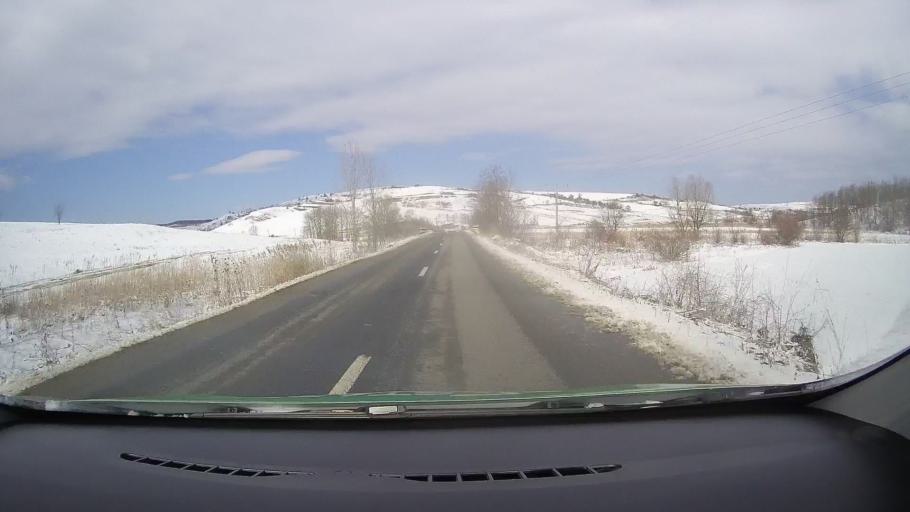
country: RO
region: Sibiu
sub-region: Comuna Altina
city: Altina
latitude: 45.9749
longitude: 24.4657
